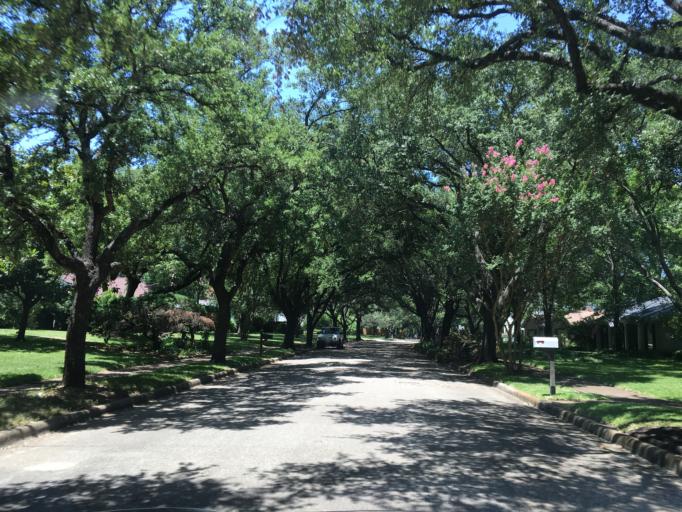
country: US
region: Texas
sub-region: Dallas County
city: Highland Park
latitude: 32.8390
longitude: -96.7348
